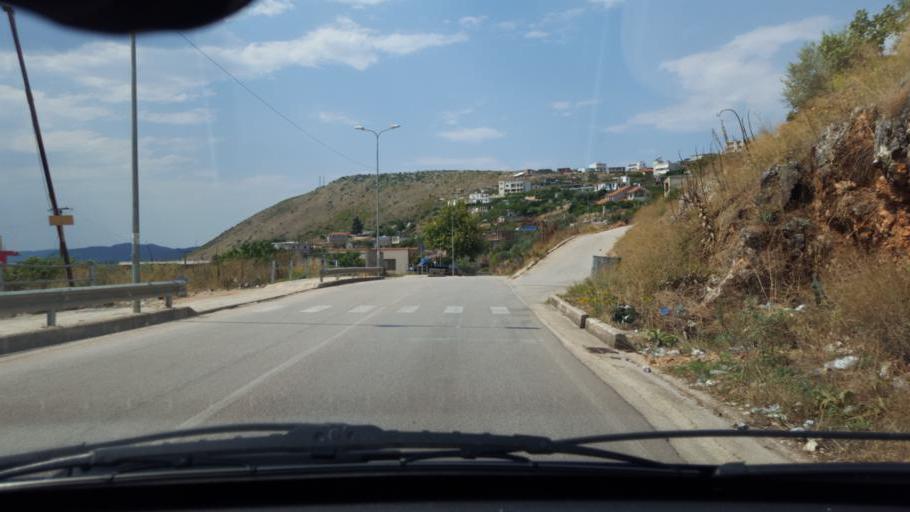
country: AL
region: Vlore
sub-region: Rrethi i Sarandes
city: Sarande
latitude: 39.8406
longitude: 20.0249
